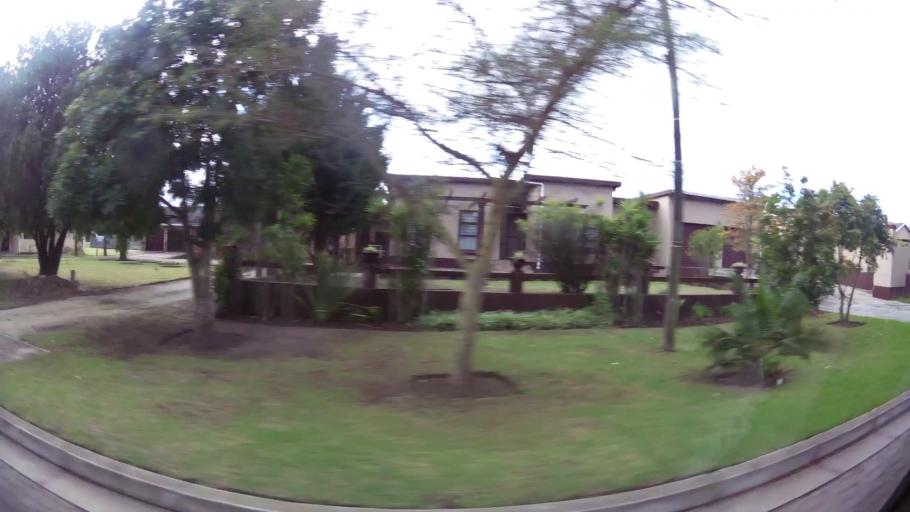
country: ZA
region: Western Cape
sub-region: Eden District Municipality
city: George
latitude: -34.0028
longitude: 22.4430
